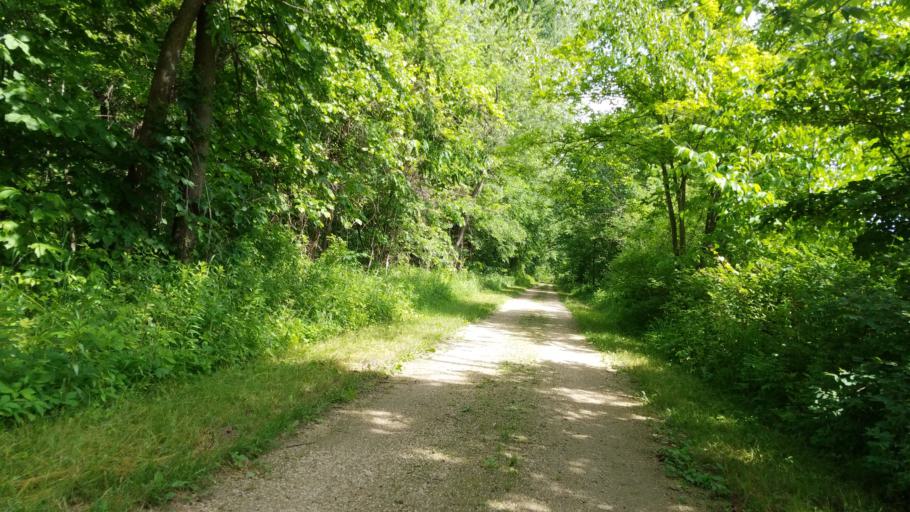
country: US
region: Wisconsin
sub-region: Dunn County
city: Menomonie
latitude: 44.8010
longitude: -91.9470
